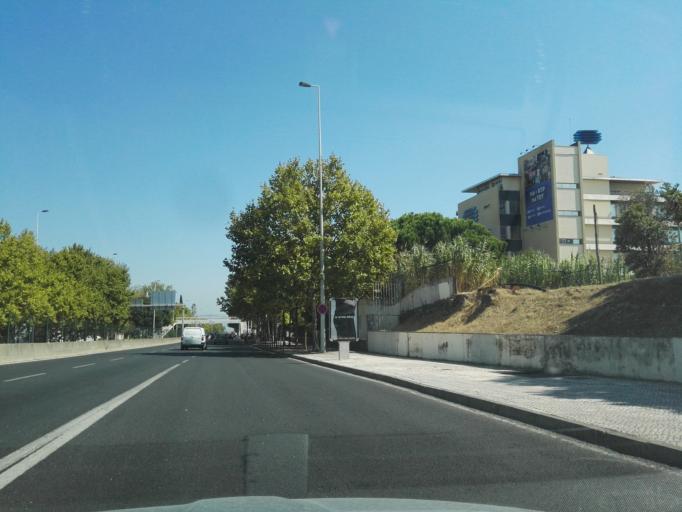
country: PT
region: Lisbon
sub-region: Loures
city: Moscavide
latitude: 38.7604
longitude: -9.1186
